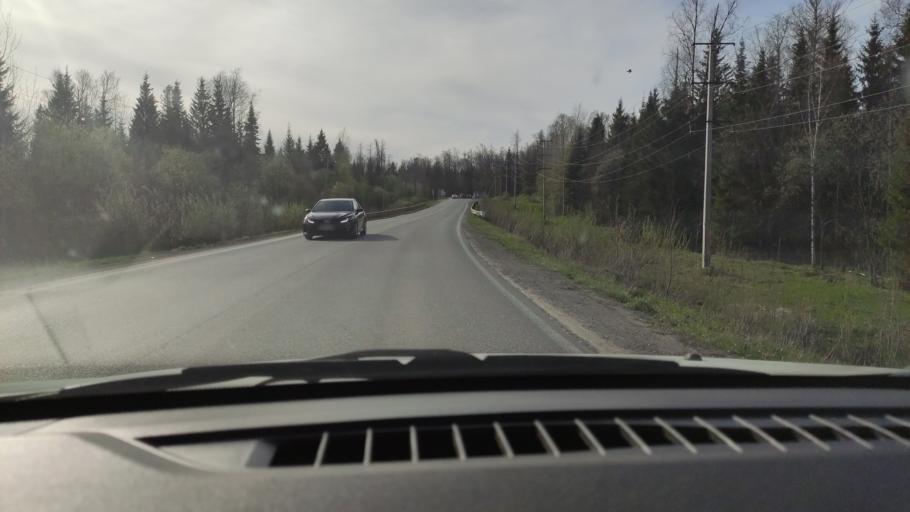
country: RU
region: Perm
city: Novyye Lyady
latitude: 57.9539
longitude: 56.5198
